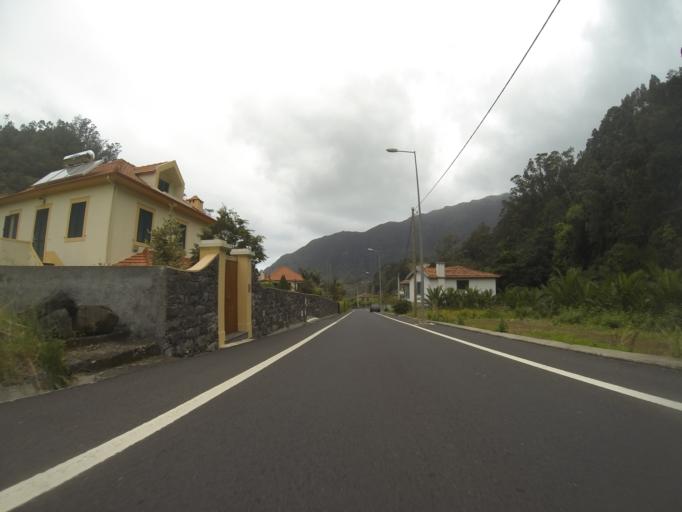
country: PT
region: Madeira
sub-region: Sao Vicente
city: Sao Vicente
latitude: 32.7836
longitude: -17.0325
